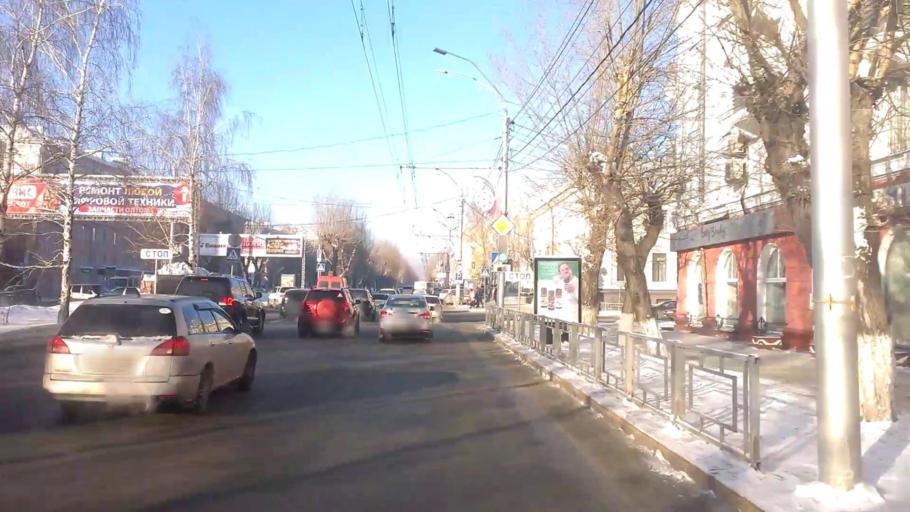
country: RU
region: Altai Krai
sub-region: Gorod Barnaulskiy
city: Barnaul
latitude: 53.3484
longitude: 83.7769
